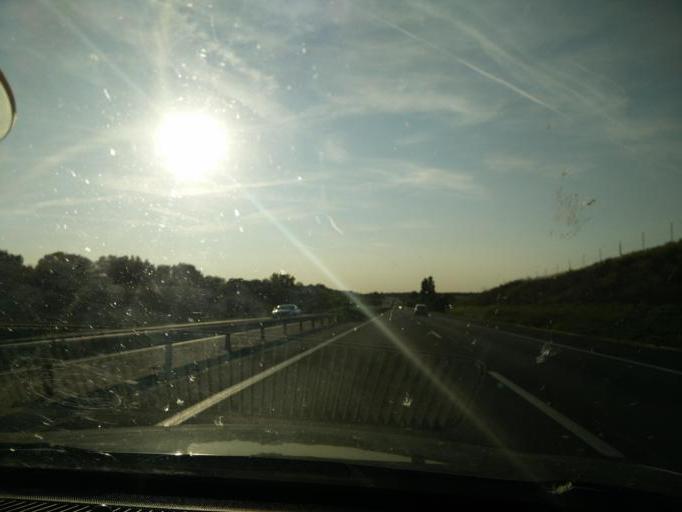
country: HU
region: Pest
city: Biatorbagy
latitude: 47.5038
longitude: 18.7741
